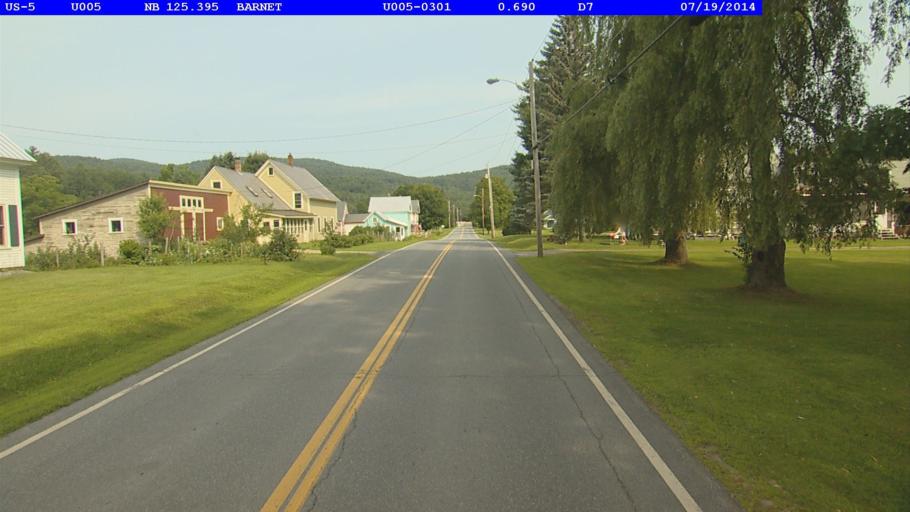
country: US
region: New Hampshire
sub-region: Grafton County
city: Woodsville
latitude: 44.2657
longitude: -72.0665
